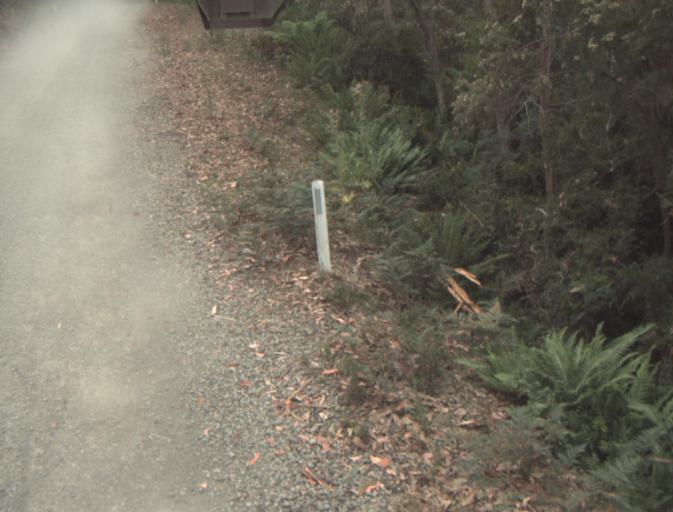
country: AU
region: Tasmania
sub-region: Dorset
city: Scottsdale
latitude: -41.4204
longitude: 147.5195
